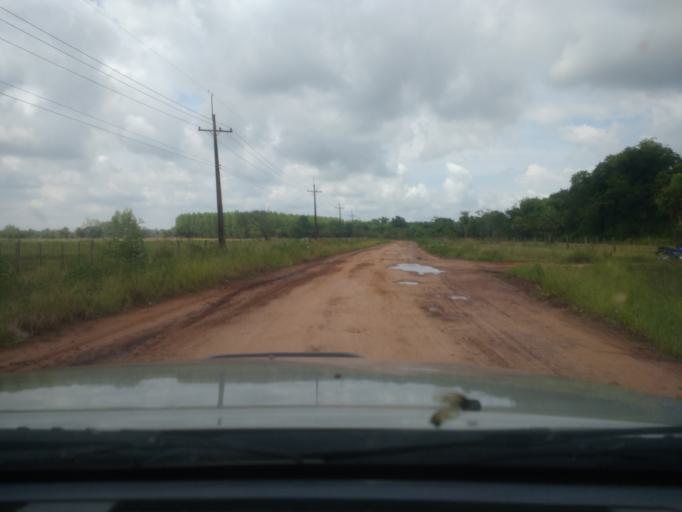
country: PY
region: San Pedro
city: Puerto Rosario
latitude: -24.3943
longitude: -57.1045
